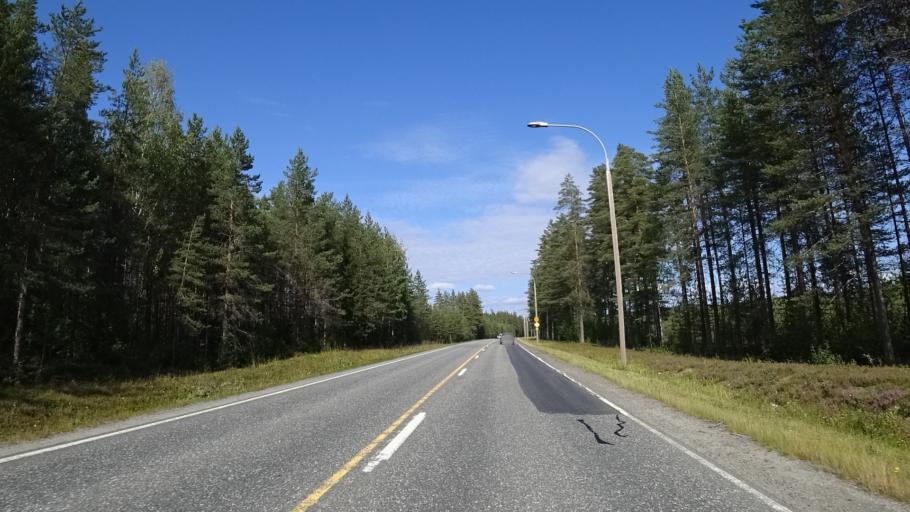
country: FI
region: North Karelia
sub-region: Joensuu
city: Eno
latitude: 62.7721
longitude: 30.0507
